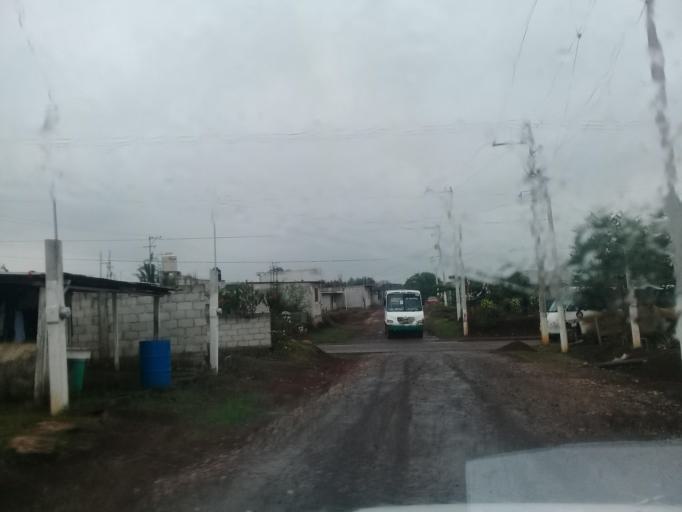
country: MX
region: Veracruz
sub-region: Cordoba
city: San Jose de Tapia
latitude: 18.8504
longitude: -96.9565
